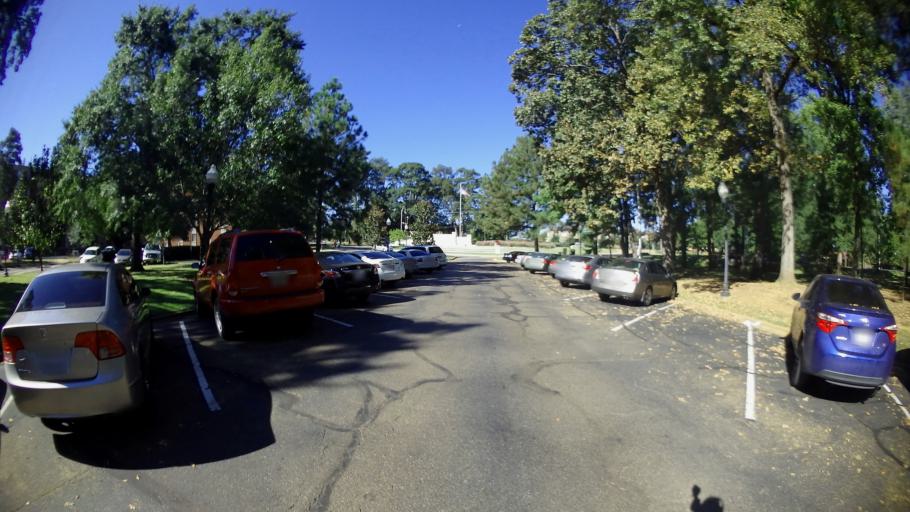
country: US
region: Texas
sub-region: Nacogdoches County
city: Nacogdoches
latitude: 31.6191
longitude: -94.6517
